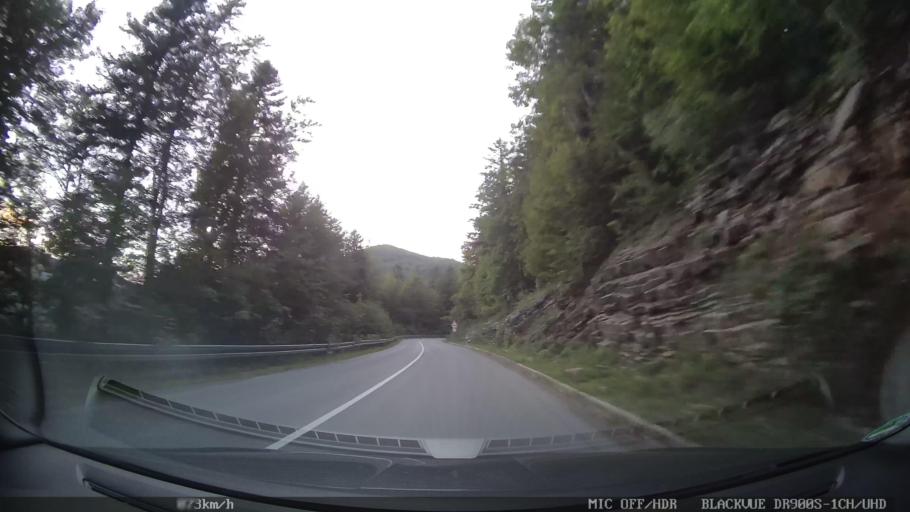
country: HR
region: Primorsko-Goranska
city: Novi Vinodolski
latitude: 45.1637
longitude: 14.9483
